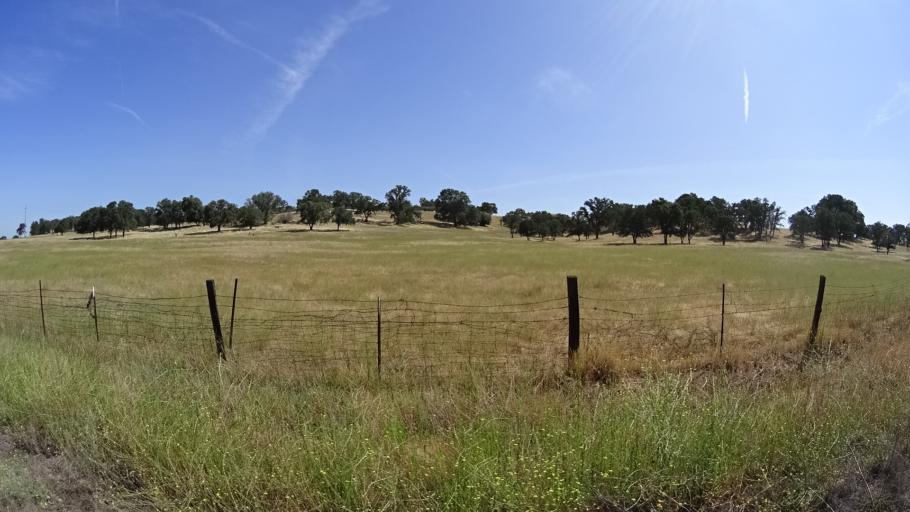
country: US
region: California
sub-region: Calaveras County
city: Rancho Calaveras
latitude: 38.1075
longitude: -120.9243
